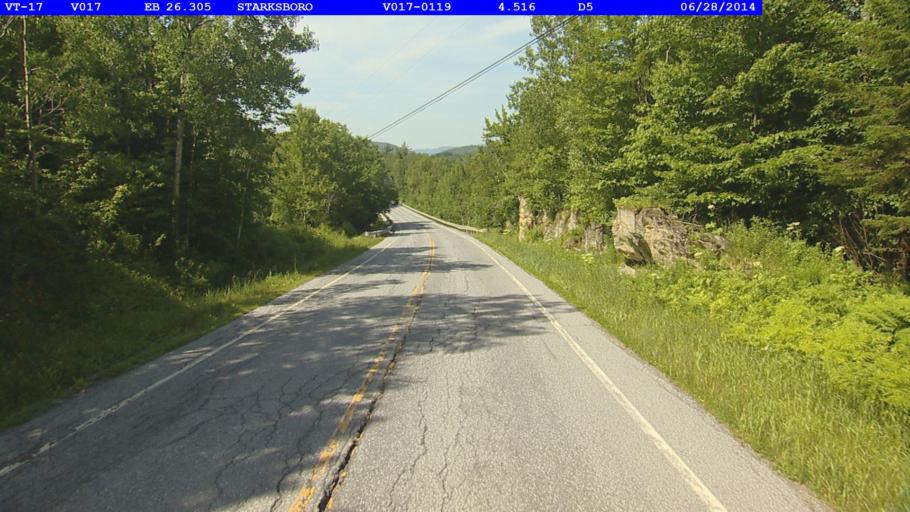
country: US
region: Vermont
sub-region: Addison County
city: Bristol
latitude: 44.2043
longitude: -72.9647
